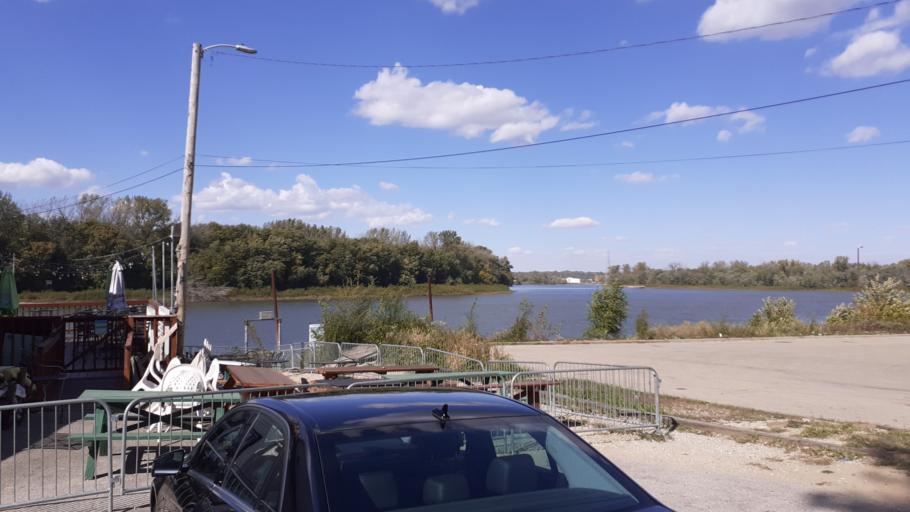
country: US
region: Illinois
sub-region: Tazewell County
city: Creve Coeur
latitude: 40.6482
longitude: -89.6095
